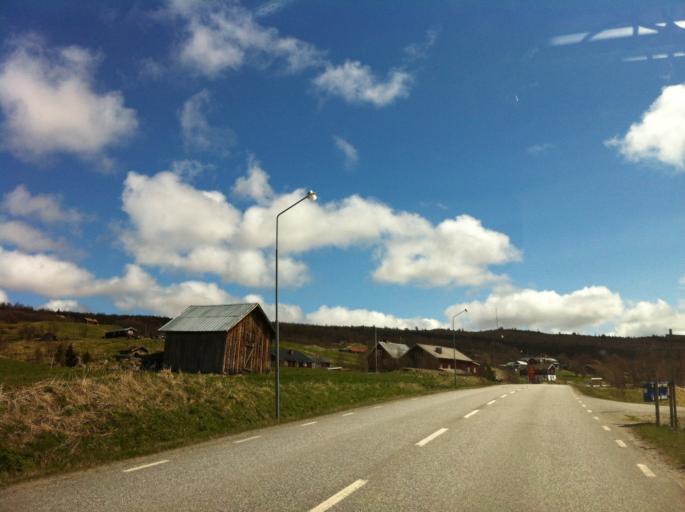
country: NO
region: Sor-Trondelag
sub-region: Tydal
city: Aas
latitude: 62.6408
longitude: 12.4365
